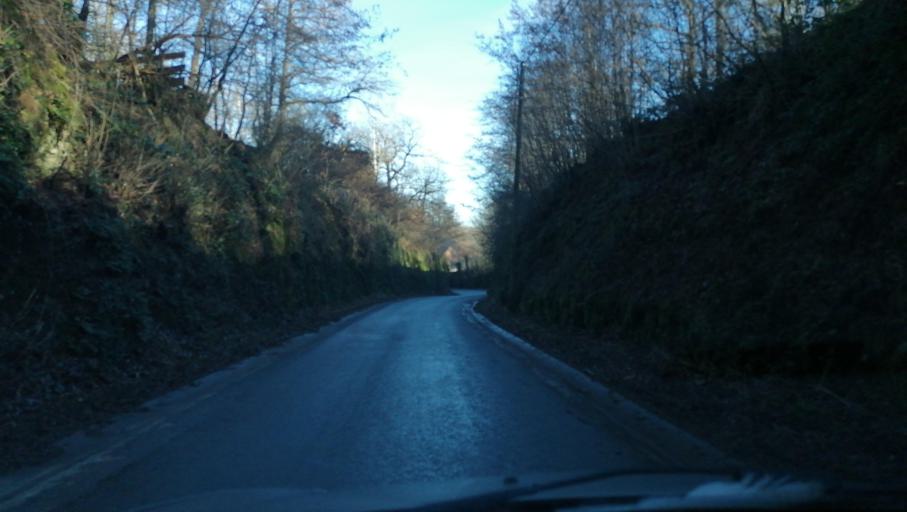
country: FR
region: Nord-Pas-de-Calais
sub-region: Departement du Nord
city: Recquignies
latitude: 50.2030
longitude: 4.0627
